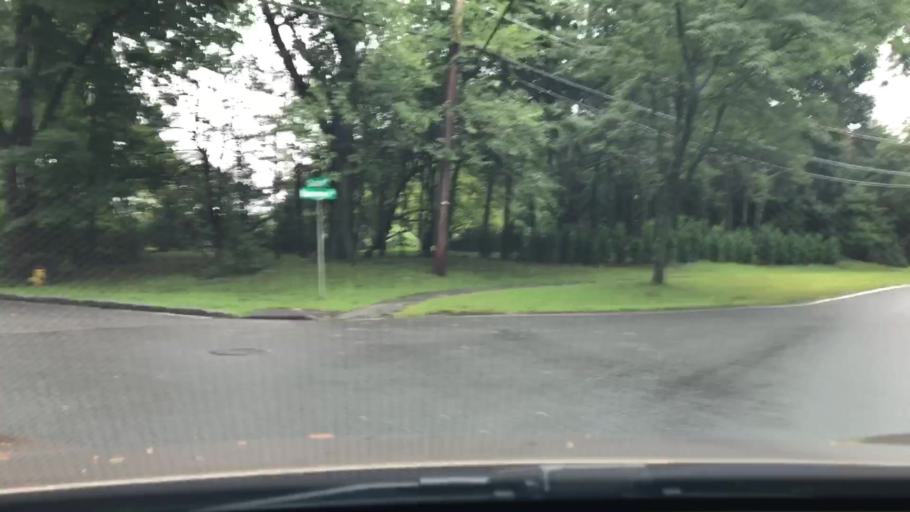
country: US
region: New York
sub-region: Westchester County
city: Scarsdale
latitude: 41.0040
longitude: -73.7804
